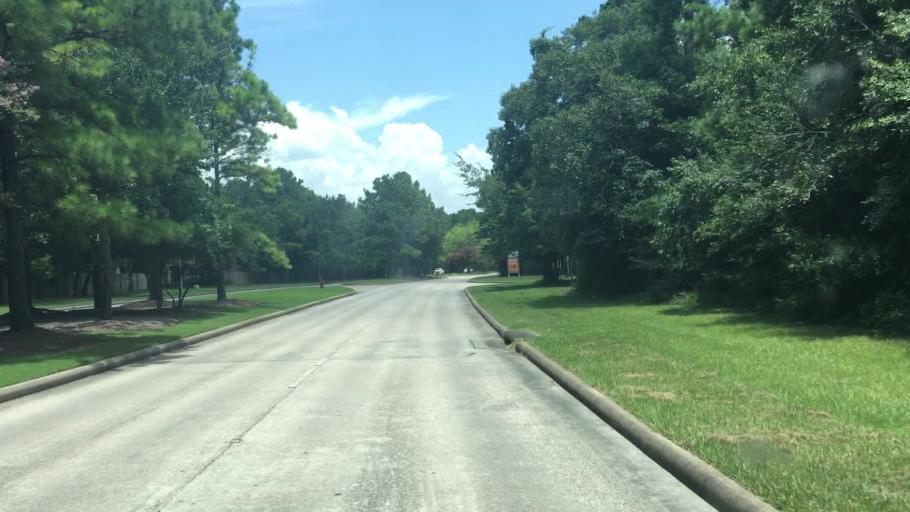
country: US
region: Texas
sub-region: Harris County
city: Atascocita
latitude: 29.9836
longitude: -95.1909
